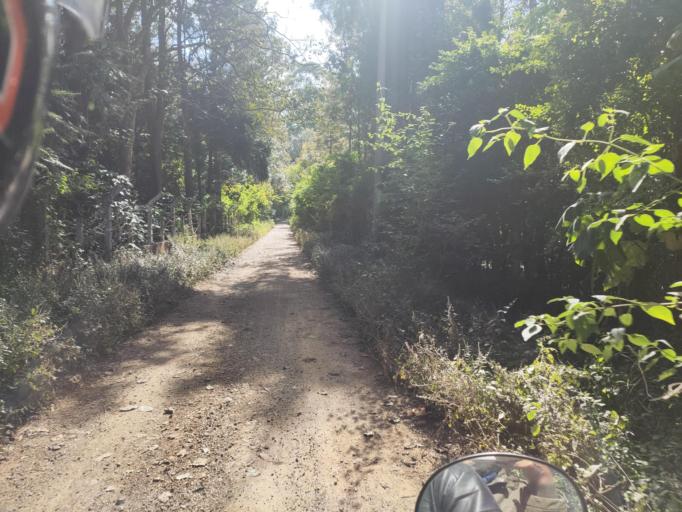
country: MM
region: Mandalay
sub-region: Pyin Oo Lwin District
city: Pyin Oo Lwin
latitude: 21.9869
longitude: 96.4665
